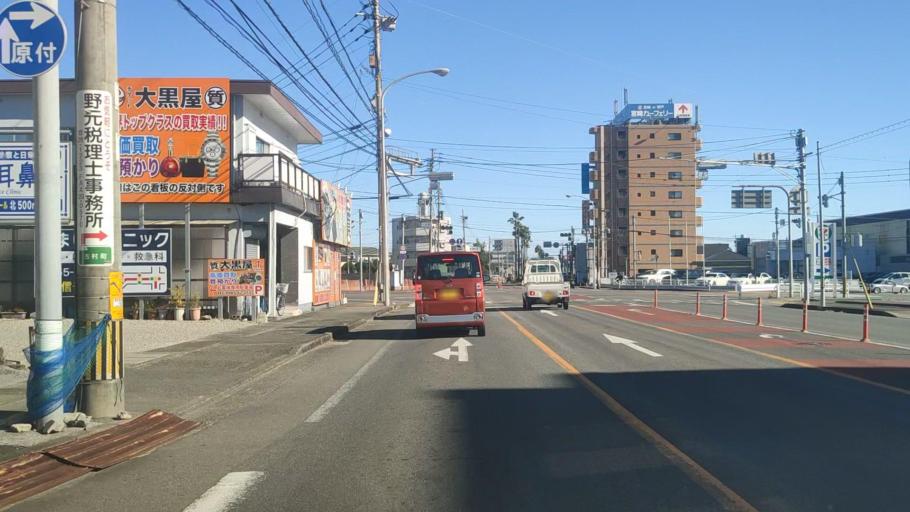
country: JP
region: Miyazaki
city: Miyazaki-shi
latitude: 31.9075
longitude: 131.4464
